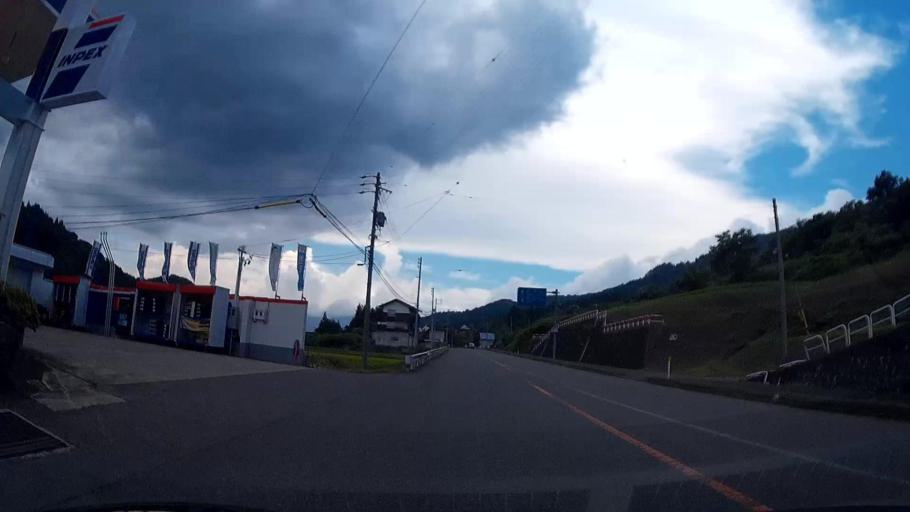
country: JP
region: Nagano
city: Iiyama
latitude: 36.9852
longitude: 138.5404
